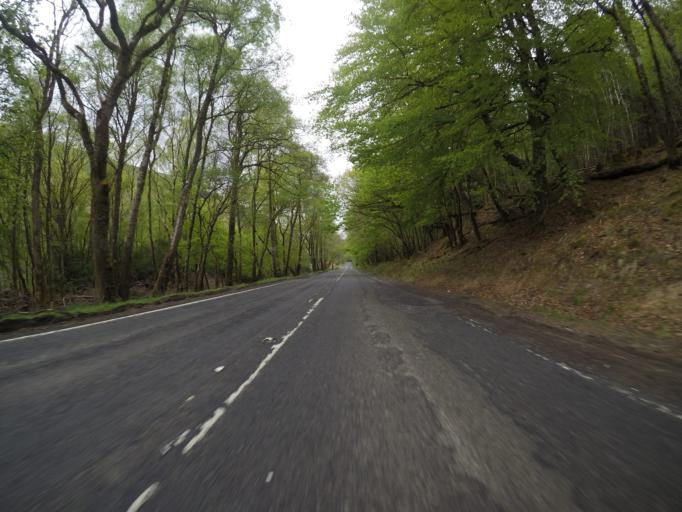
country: GB
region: Scotland
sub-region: Highland
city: Spean Bridge
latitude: 57.0592
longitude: -4.7868
